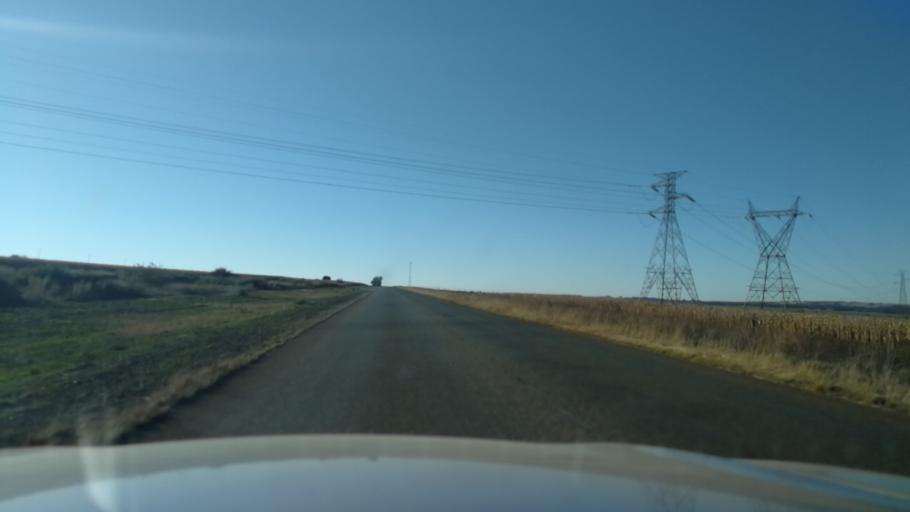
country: ZA
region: North-West
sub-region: Bojanala Platinum District Municipality
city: Rustenburg
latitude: -25.9966
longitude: 27.2986
